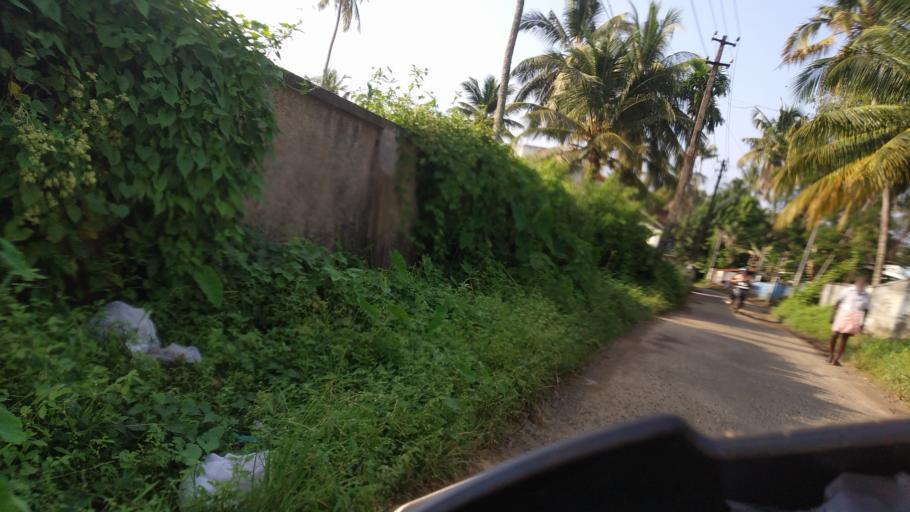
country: IN
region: Kerala
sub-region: Ernakulam
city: Elur
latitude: 10.0395
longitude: 76.2284
